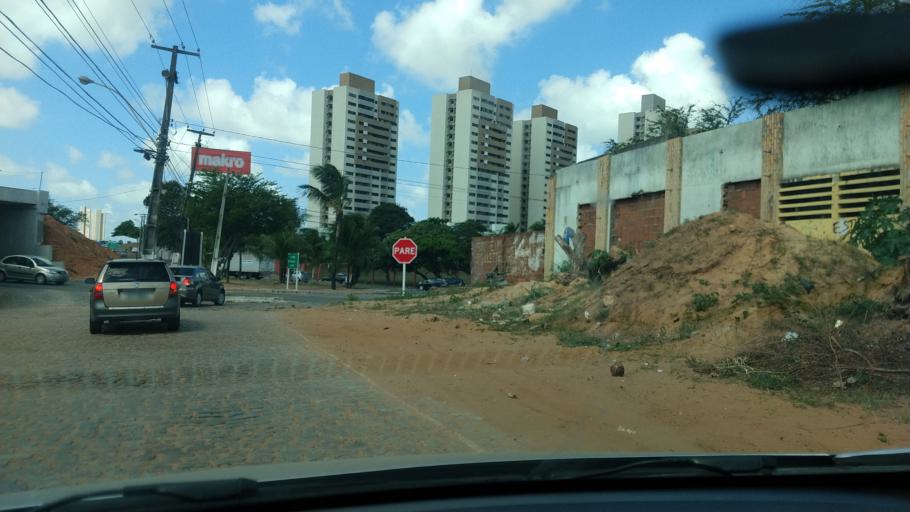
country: BR
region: Rio Grande do Norte
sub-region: Natal
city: Natal
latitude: -5.8626
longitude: -35.2148
